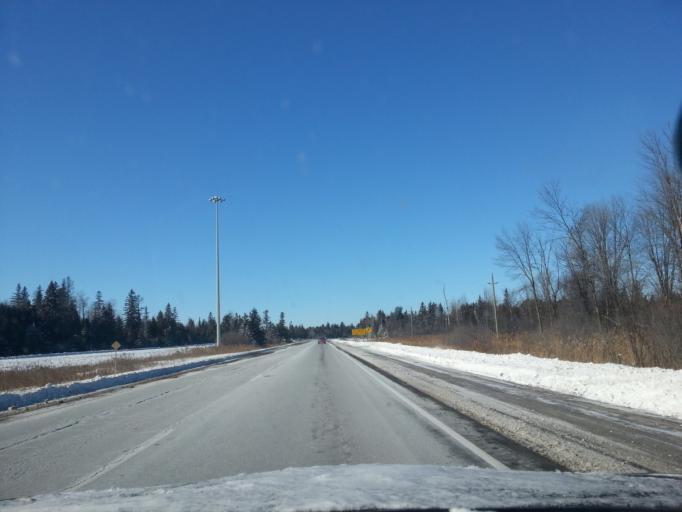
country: CA
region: Ontario
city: Bells Corners
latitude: 45.2723
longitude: -75.9802
